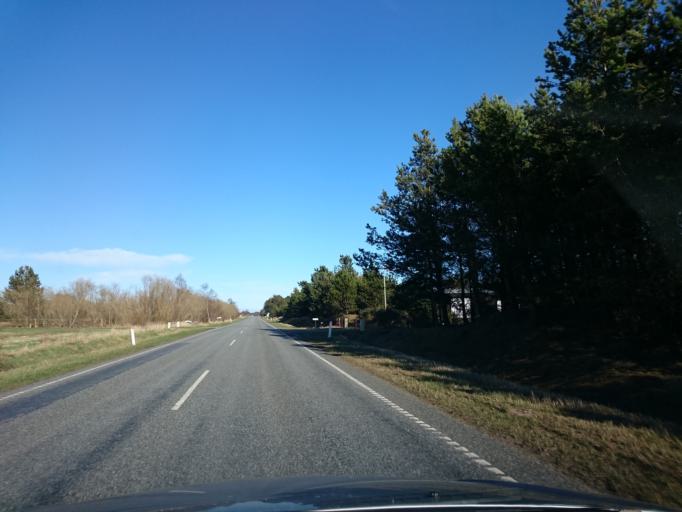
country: DK
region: North Denmark
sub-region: Frederikshavn Kommune
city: Strandby
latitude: 57.6058
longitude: 10.3550
